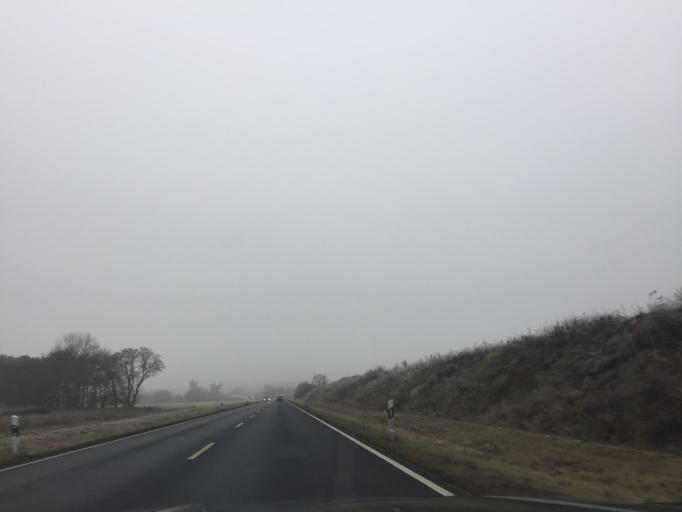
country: DE
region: Brandenburg
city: Falkensee
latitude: 52.6184
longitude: 13.1328
